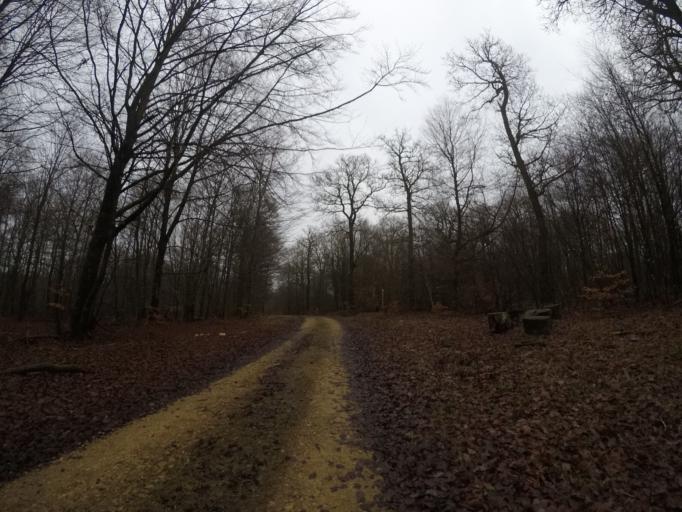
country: BE
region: Wallonia
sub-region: Province du Luxembourg
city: Fauvillers
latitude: 49.8139
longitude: 5.6341
